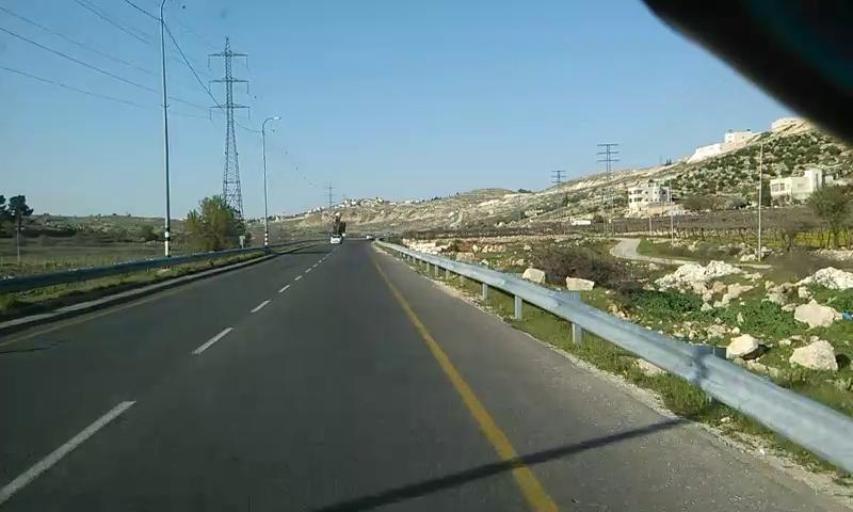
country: PS
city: Al Buq`ah
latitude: 31.5484
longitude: 35.1342
